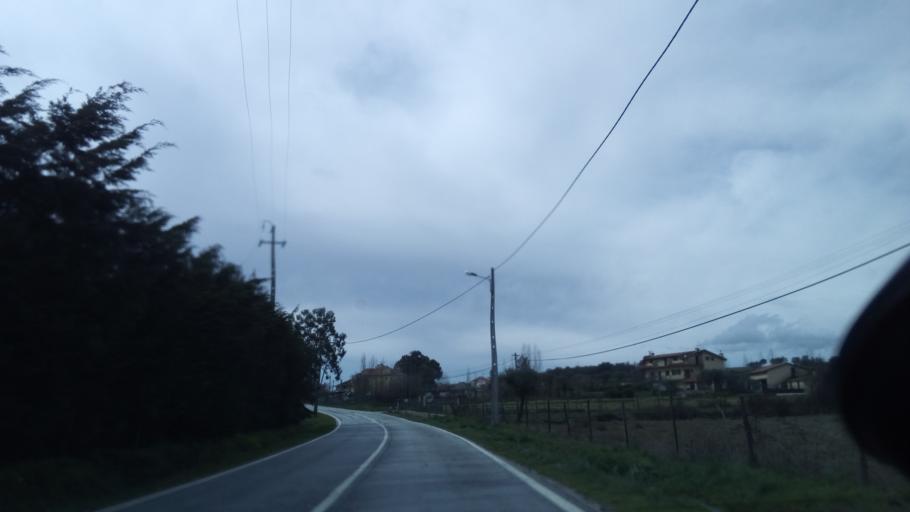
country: PT
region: Guarda
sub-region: Seia
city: Seia
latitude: 40.4520
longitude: -7.7062
